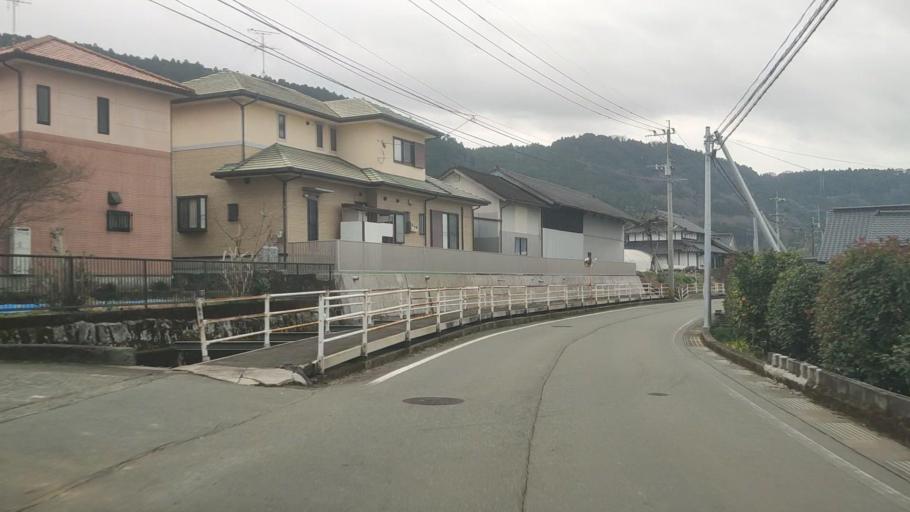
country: JP
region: Kumamoto
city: Ozu
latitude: 32.8562
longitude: 130.8841
